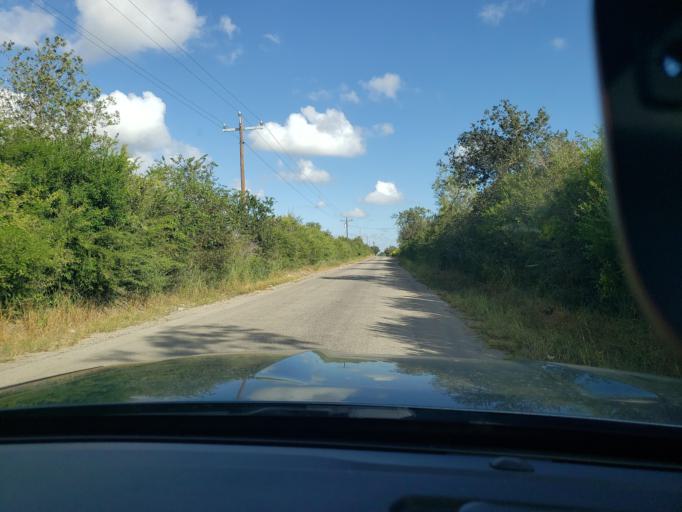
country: US
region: Texas
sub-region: Bee County
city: Beeville
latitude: 28.4556
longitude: -97.7180
